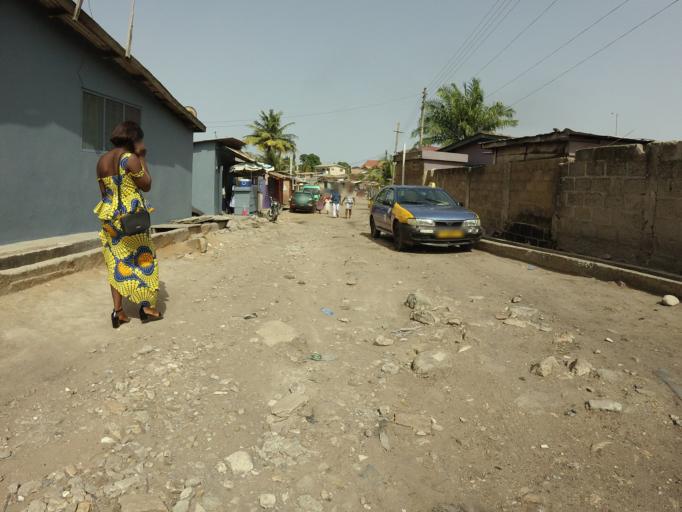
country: GH
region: Greater Accra
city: Dome
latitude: 5.6146
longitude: -0.2390
